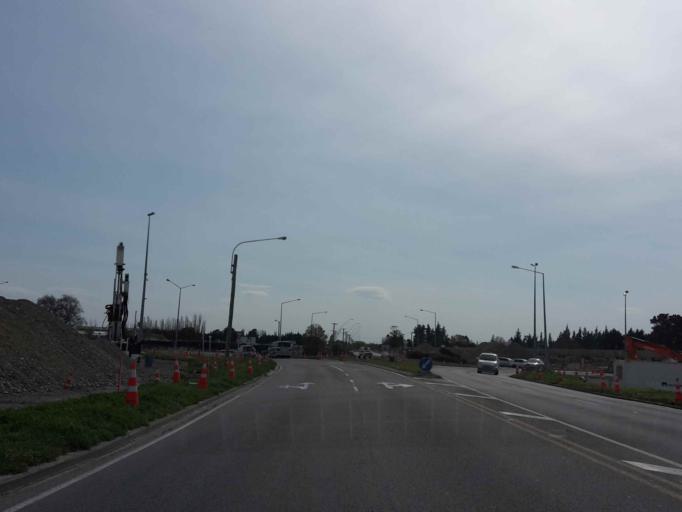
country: NZ
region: Canterbury
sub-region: Christchurch City
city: Christchurch
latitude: -43.4941
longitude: 172.5493
